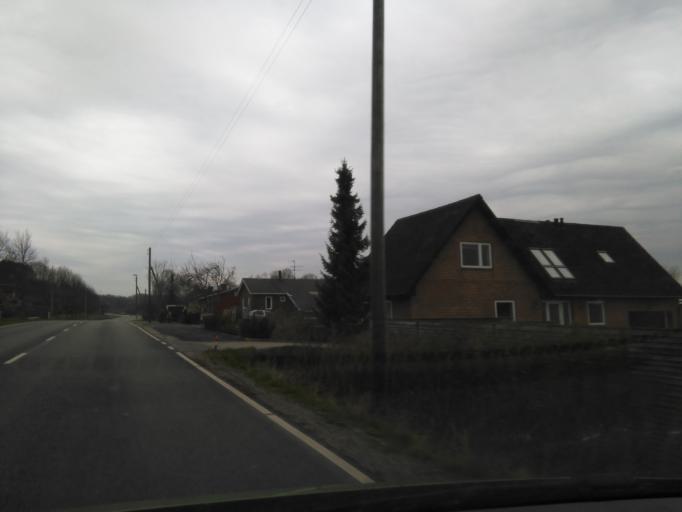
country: DK
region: North Denmark
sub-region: Mariagerfjord Kommune
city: Hadsund
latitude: 56.7034
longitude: 10.1153
